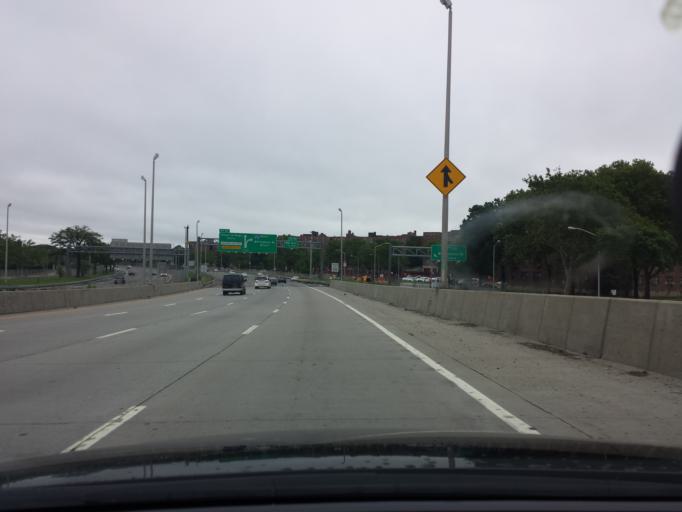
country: US
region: New York
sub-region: Queens County
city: Jamaica
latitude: 40.7720
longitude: -73.8320
